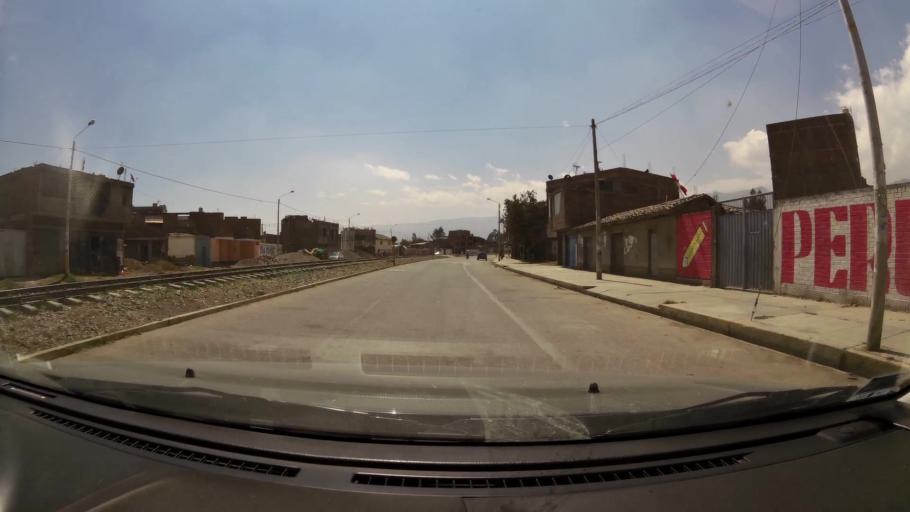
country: PE
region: Junin
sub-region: Provincia de Huancayo
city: El Tambo
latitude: -12.0862
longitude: -75.2139
